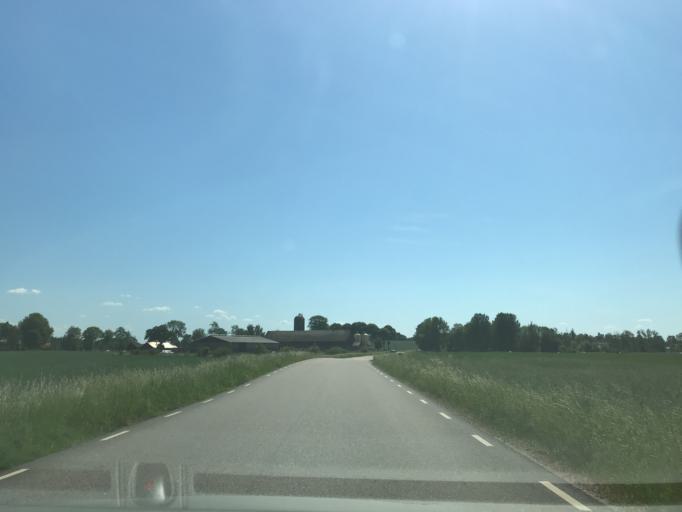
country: SE
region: Vaestra Goetaland
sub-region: Gotene Kommun
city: Kallby
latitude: 58.5175
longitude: 13.3196
